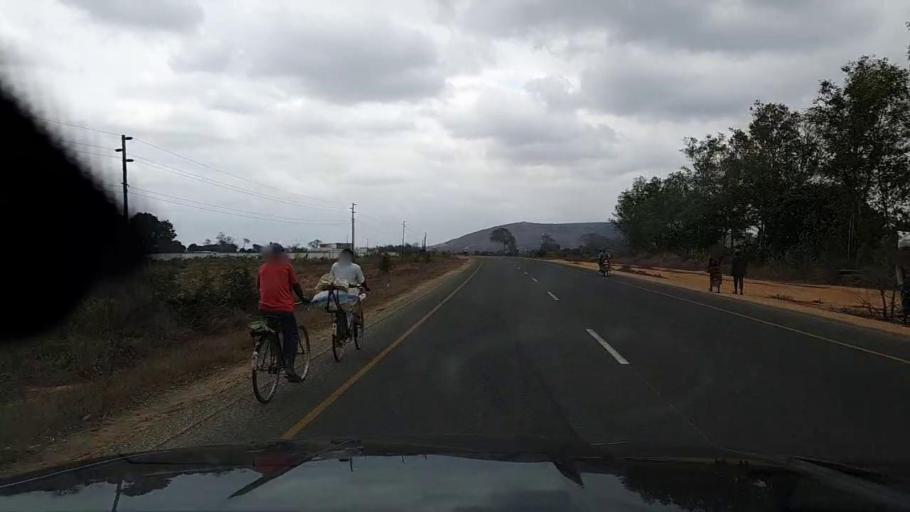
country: MZ
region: Nampula
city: Nampula
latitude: -15.1627
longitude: 39.3069
